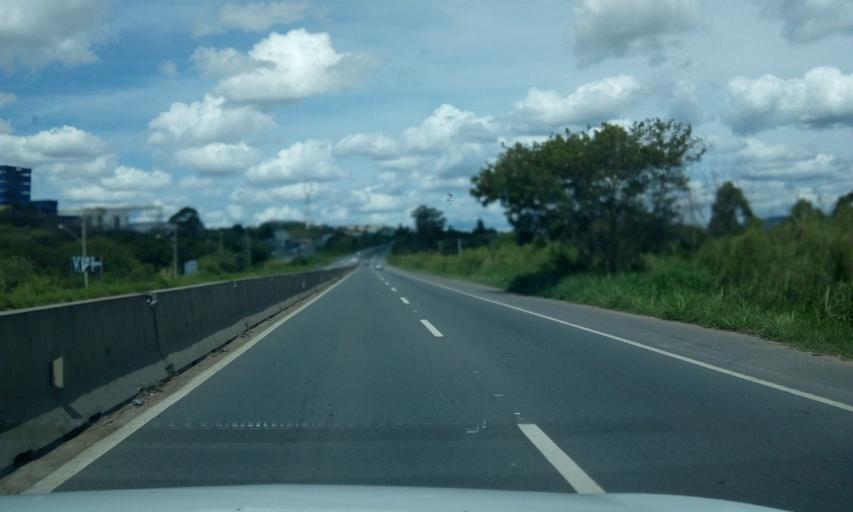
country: BR
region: Sao Paulo
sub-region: Itupeva
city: Itupeva
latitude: -23.1619
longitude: -47.0208
